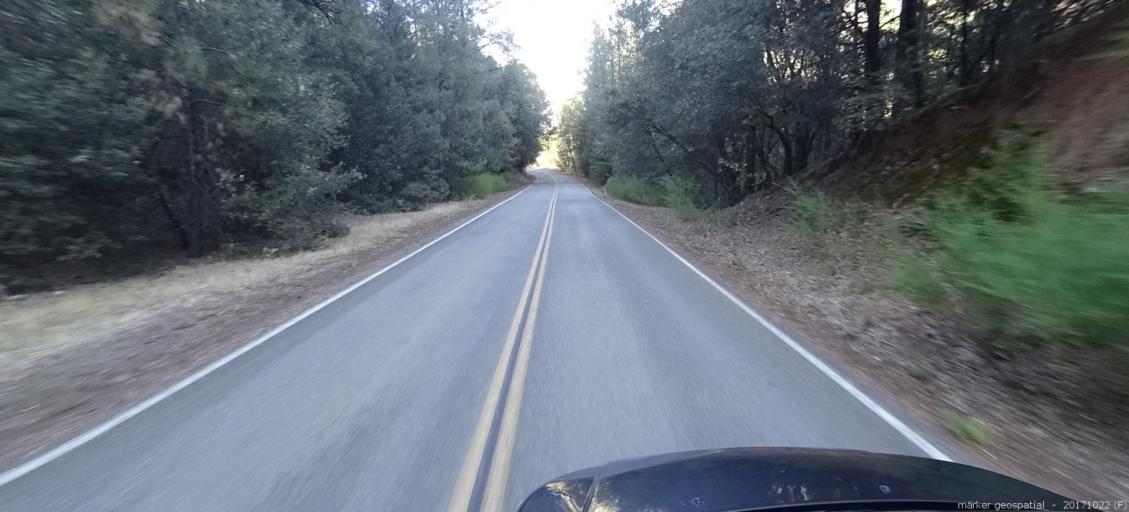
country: US
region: California
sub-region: Siskiyou County
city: Dunsmuir
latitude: 40.9339
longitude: -122.2497
